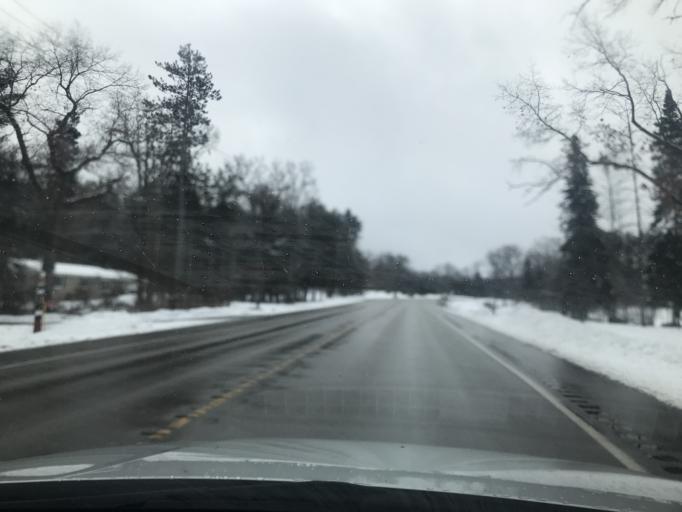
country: US
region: Wisconsin
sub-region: Marinette County
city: Peshtigo
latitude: 45.1689
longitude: -87.7325
